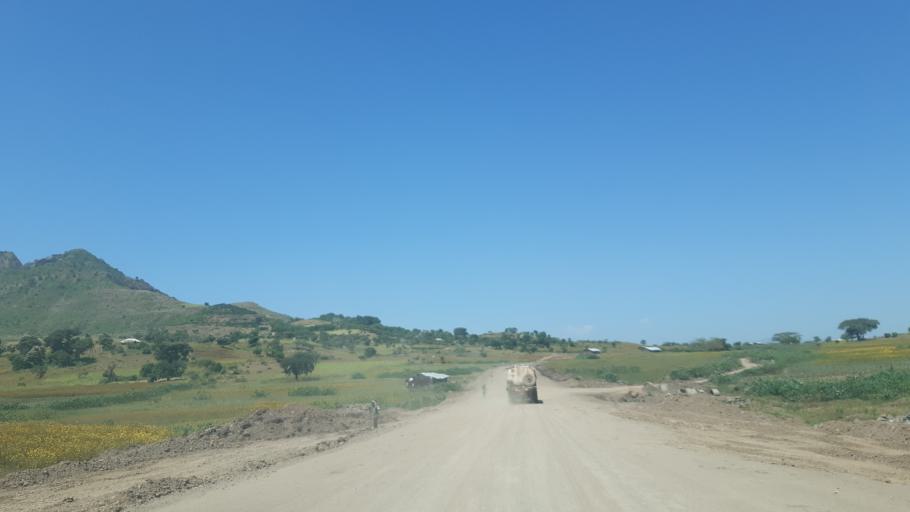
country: ET
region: Amhara
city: Dabat
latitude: 13.1577
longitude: 37.6108
